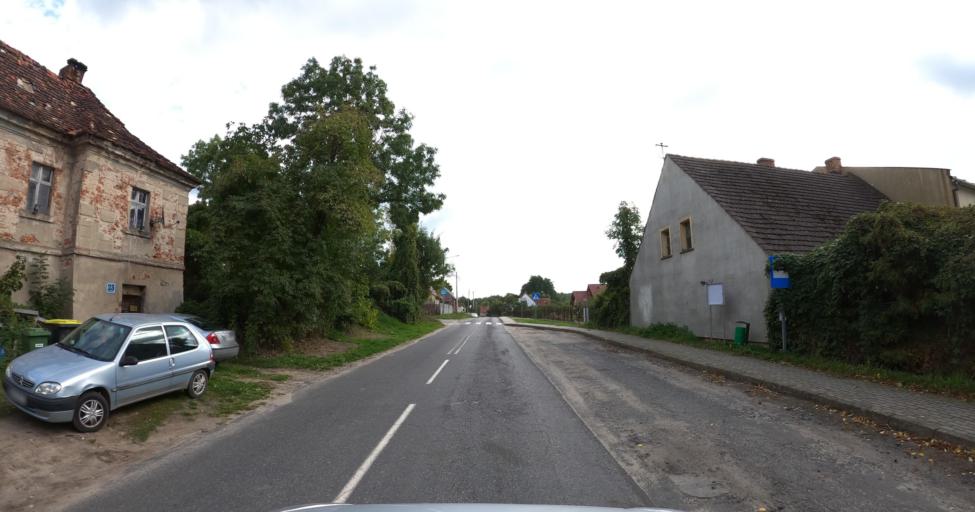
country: PL
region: Lubusz
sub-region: Powiat zielonogorski
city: Zabor
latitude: 51.9568
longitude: 15.6273
